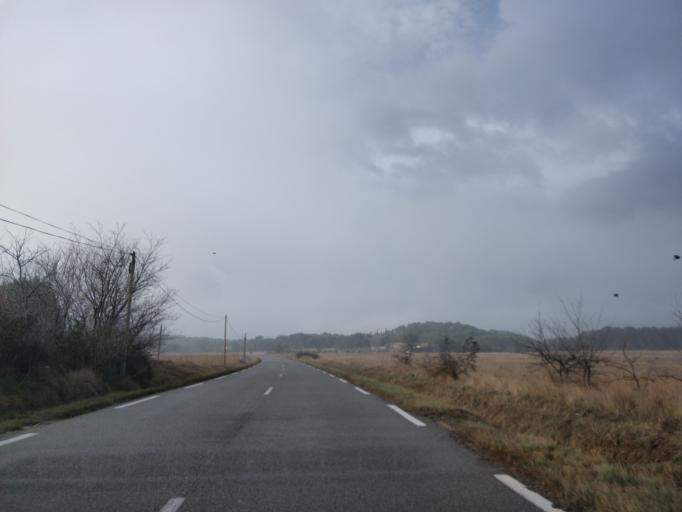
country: FR
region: Languedoc-Roussillon
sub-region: Departement du Gard
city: Nimes
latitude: 43.8706
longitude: 4.3141
